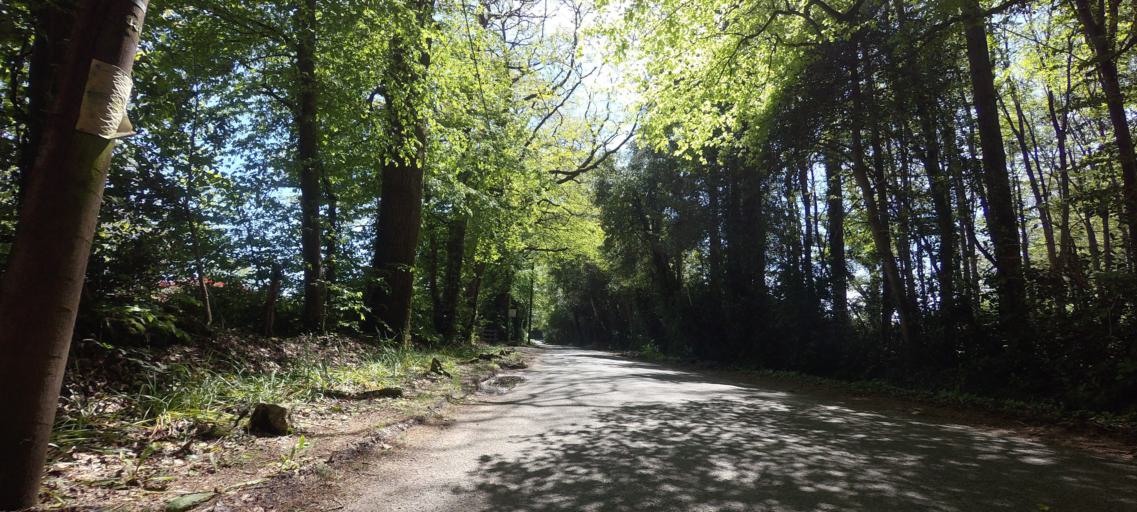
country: GB
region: England
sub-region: Dorset
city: Bovington Camp
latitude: 50.6878
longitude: -2.3183
